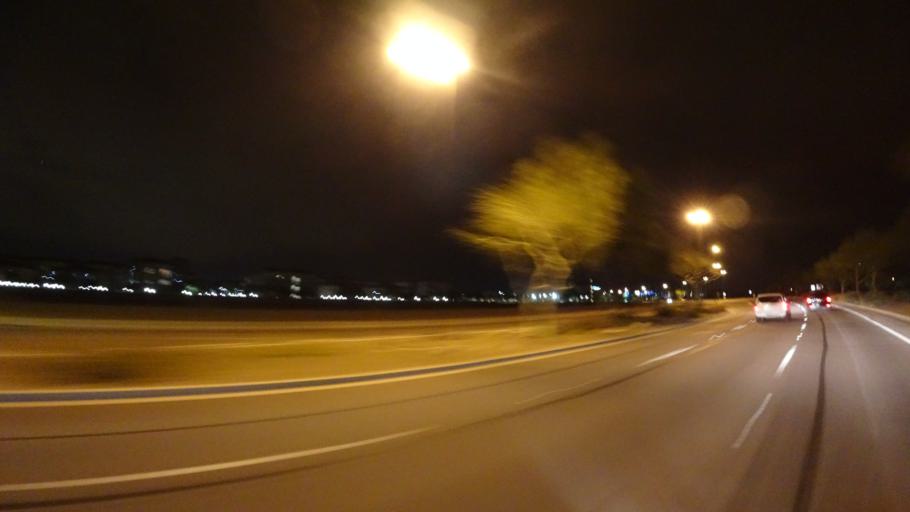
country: US
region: Arizona
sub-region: Maricopa County
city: Gilbert
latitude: 33.3140
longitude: -111.7444
